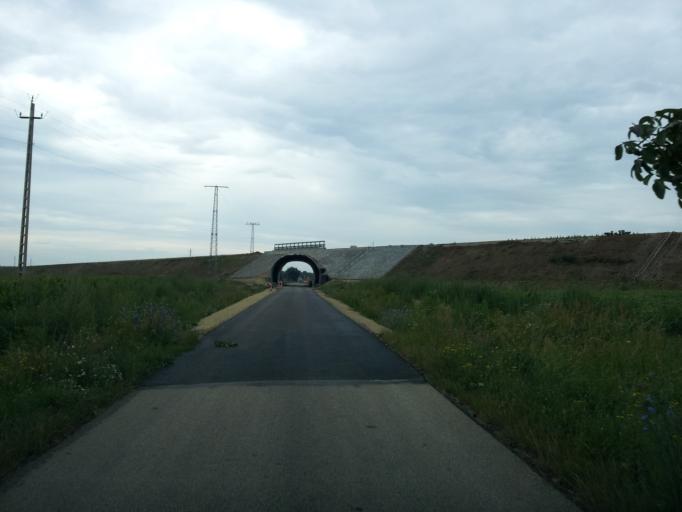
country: HU
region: Vas
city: Kormend
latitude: 46.9714
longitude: 16.6225
